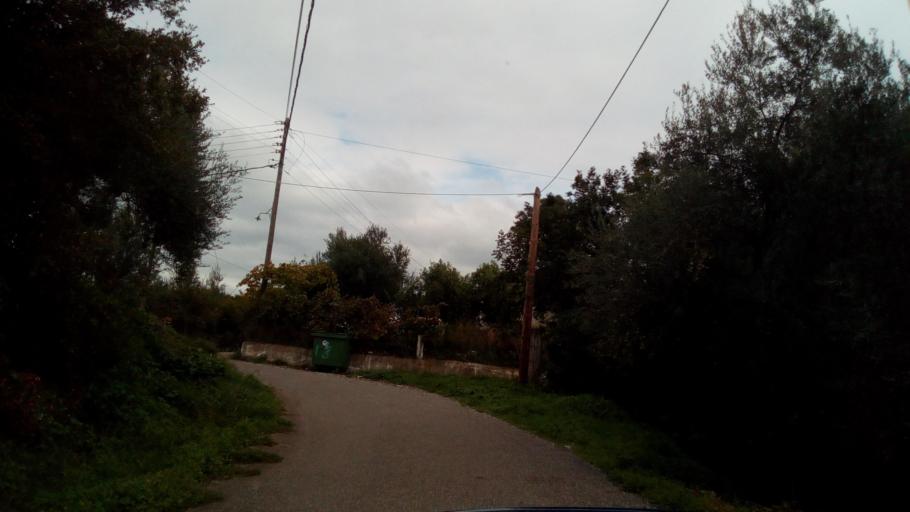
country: GR
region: West Greece
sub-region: Nomos Achaias
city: Kamarai
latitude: 38.4129
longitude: 21.9536
